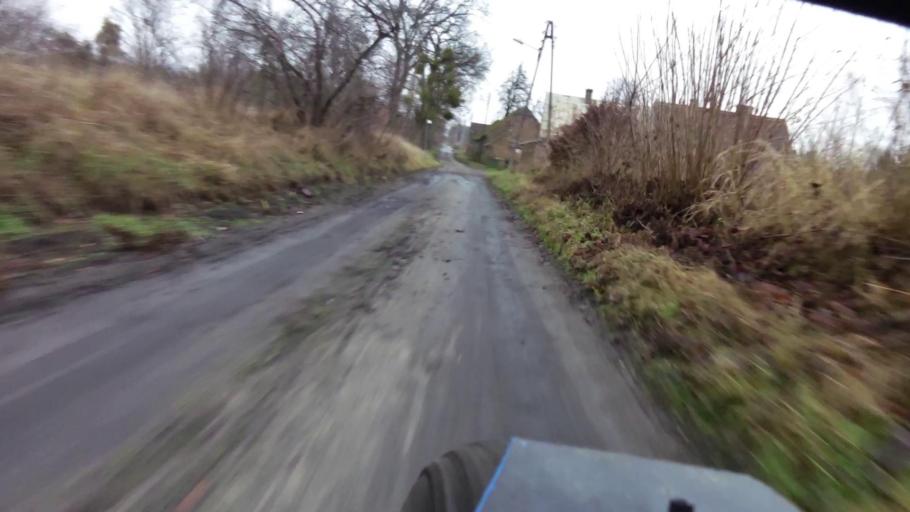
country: PL
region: Lubusz
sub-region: Powiat gorzowski
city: Witnica
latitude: 52.6797
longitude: 14.8066
